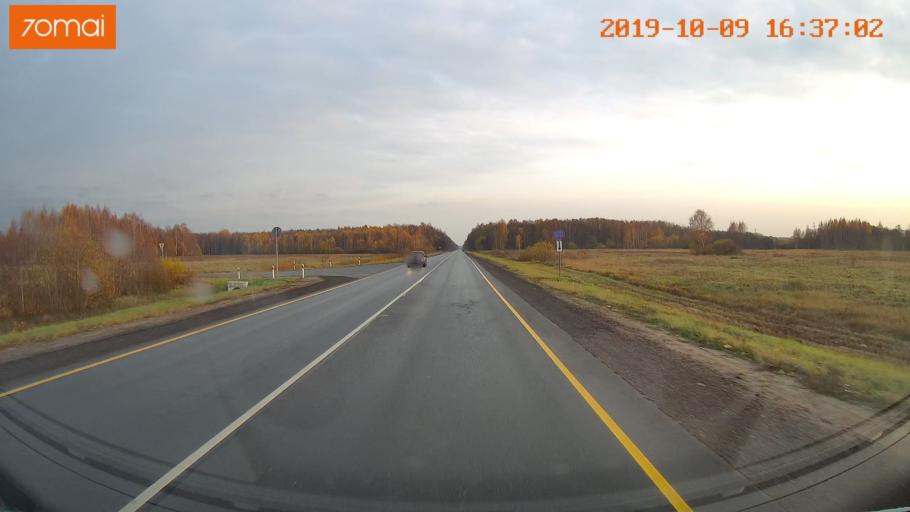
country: RU
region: Kostroma
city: Volgorechensk
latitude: 57.5330
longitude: 41.0197
